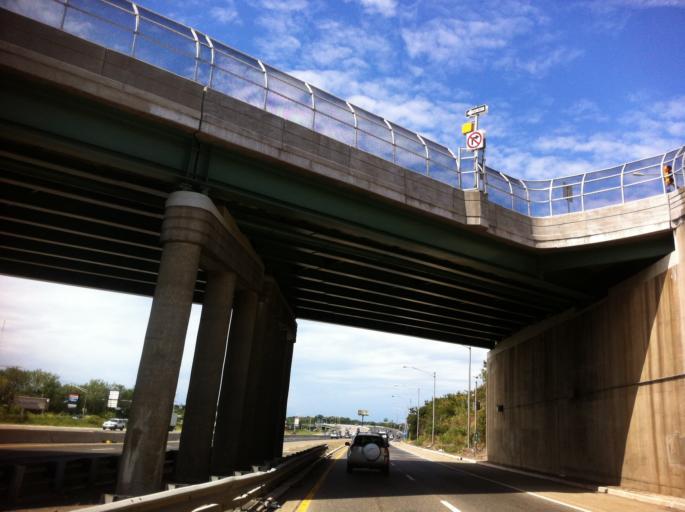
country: US
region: New Jersey
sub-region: Bergen County
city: Hackensack
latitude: 40.8722
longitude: -74.0593
